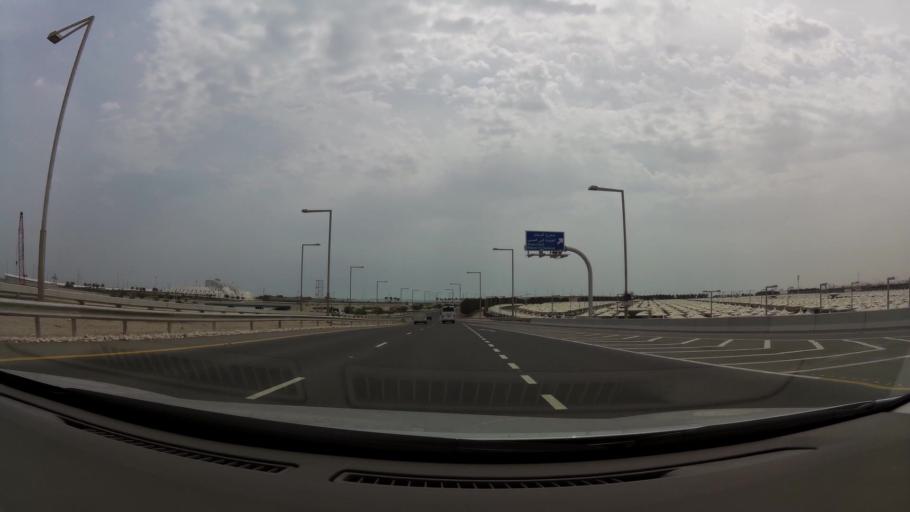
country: QA
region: Al Wakrah
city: Al Wakrah
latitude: 25.2564
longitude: 51.6138
